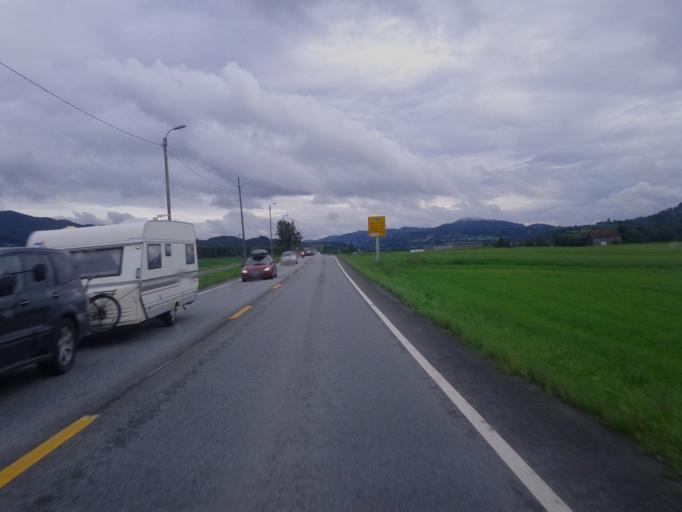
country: NO
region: Sor-Trondelag
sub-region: Melhus
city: Melhus
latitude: 63.3157
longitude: 10.2956
